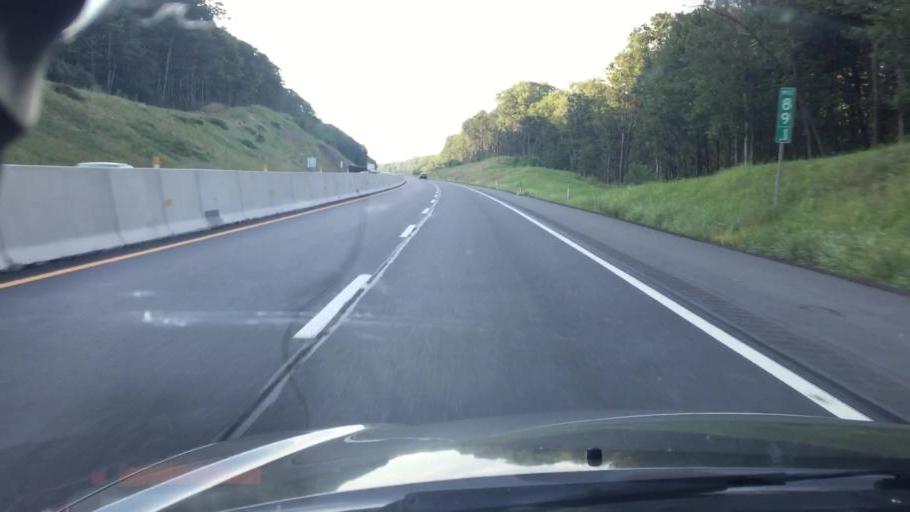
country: US
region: Pennsylvania
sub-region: Carbon County
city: Towamensing Trails
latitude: 41.0120
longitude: -75.6379
